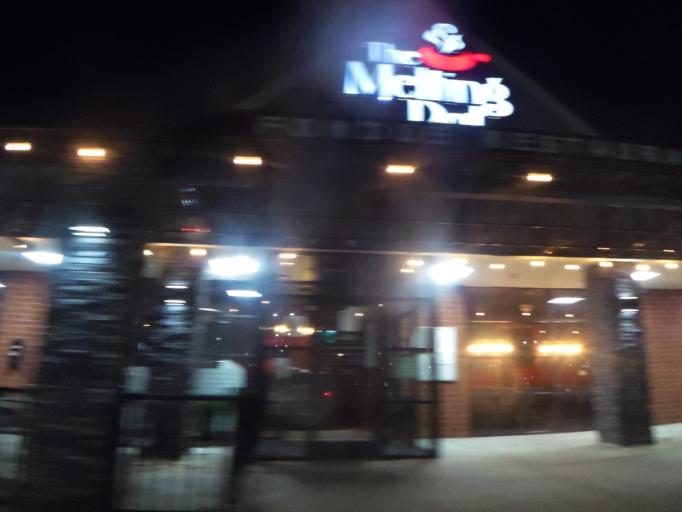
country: US
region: Virginia
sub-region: York County
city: Yorktown
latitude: 37.1103
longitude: -76.4994
